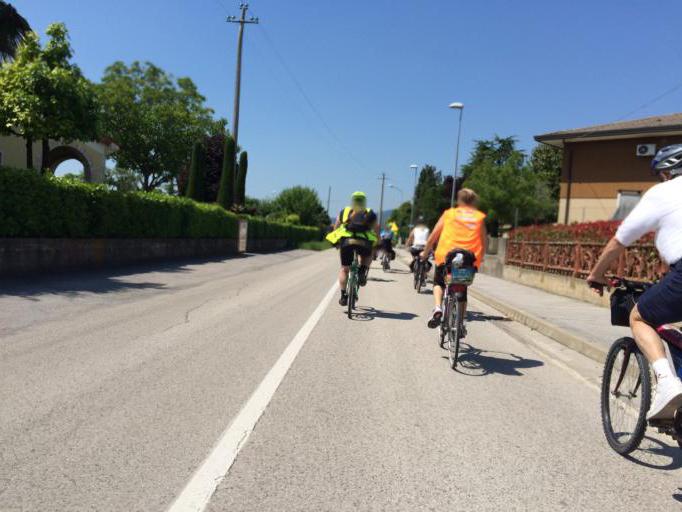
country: IT
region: Veneto
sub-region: Provincia di Vicenza
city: Villaganzerla
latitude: 45.4330
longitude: 11.6152
